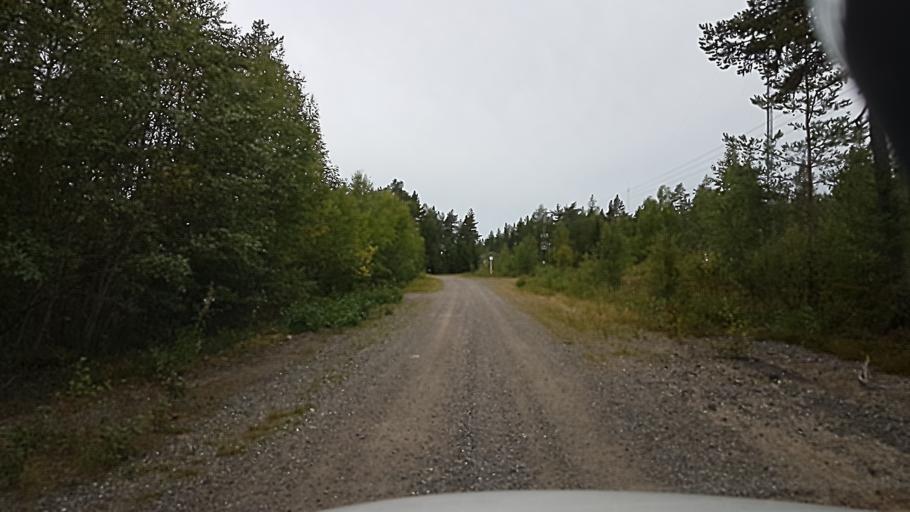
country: SE
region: Gaevleborg
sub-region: Ljusdals Kommun
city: Farila
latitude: 61.8182
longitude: 15.8475
